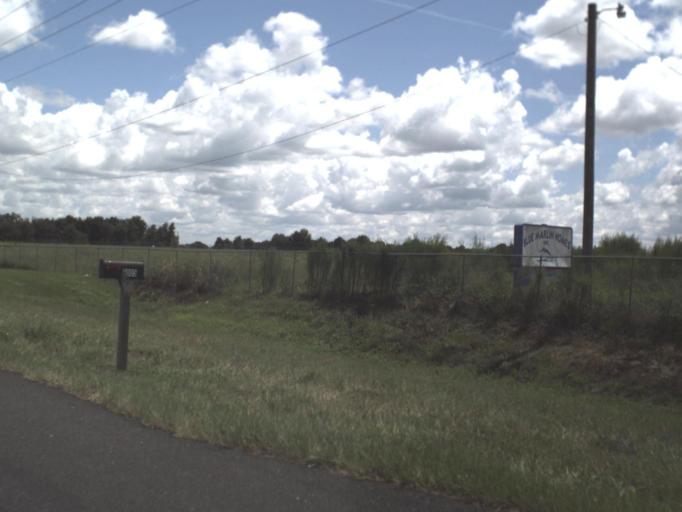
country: US
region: Florida
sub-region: Polk County
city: Wahneta
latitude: 27.9091
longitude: -81.7719
